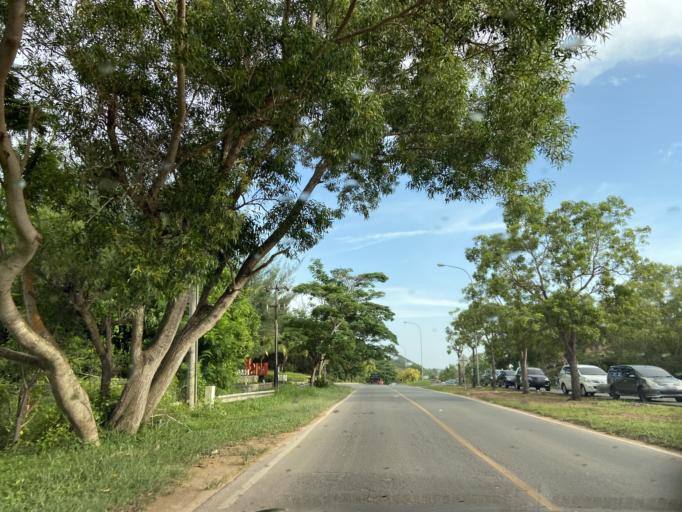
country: SG
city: Singapore
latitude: 0.9855
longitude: 104.0386
